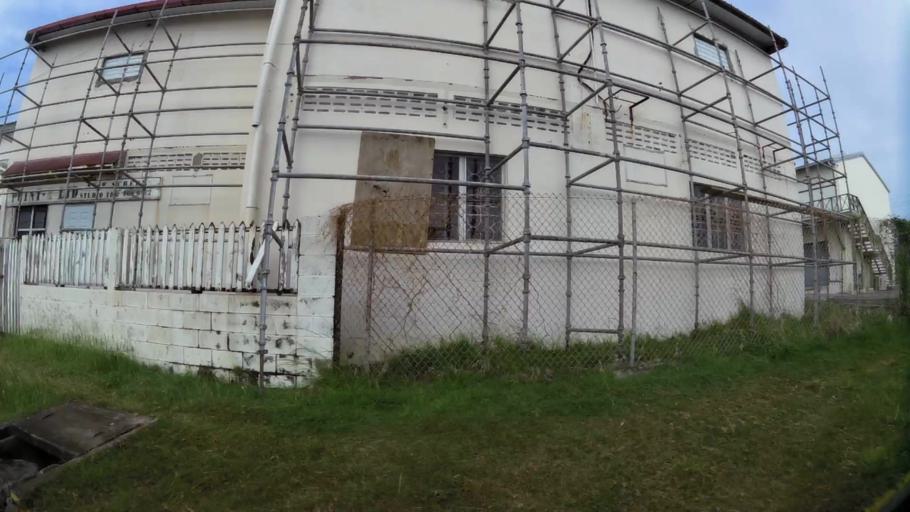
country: KN
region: Saint George Basseterre
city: Basseterre
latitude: 17.2949
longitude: -62.7139
